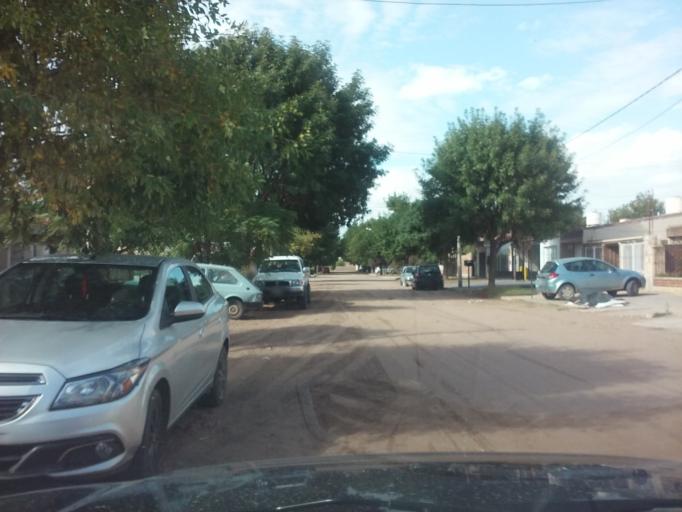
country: AR
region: La Pampa
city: Santa Rosa
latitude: -36.6501
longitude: -64.2949
